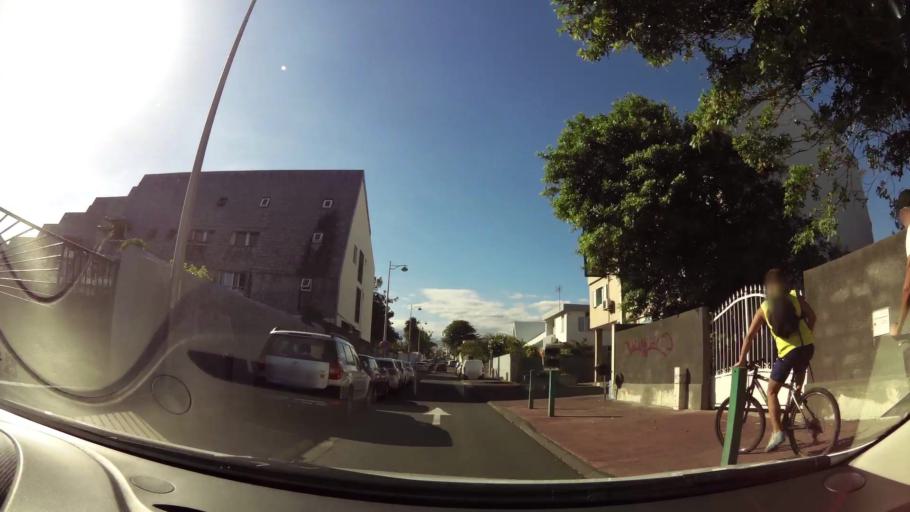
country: RE
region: Reunion
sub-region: Reunion
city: Saint-Pierre
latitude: -21.3429
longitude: 55.4695
